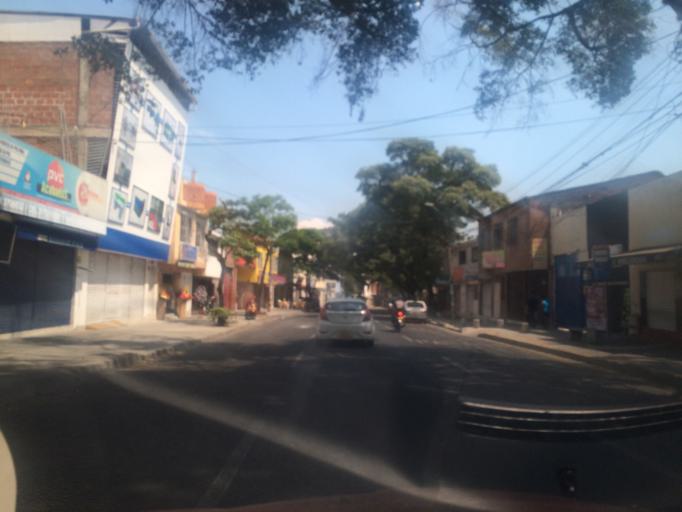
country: CO
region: Valle del Cauca
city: Cali
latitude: 3.4465
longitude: -76.5341
